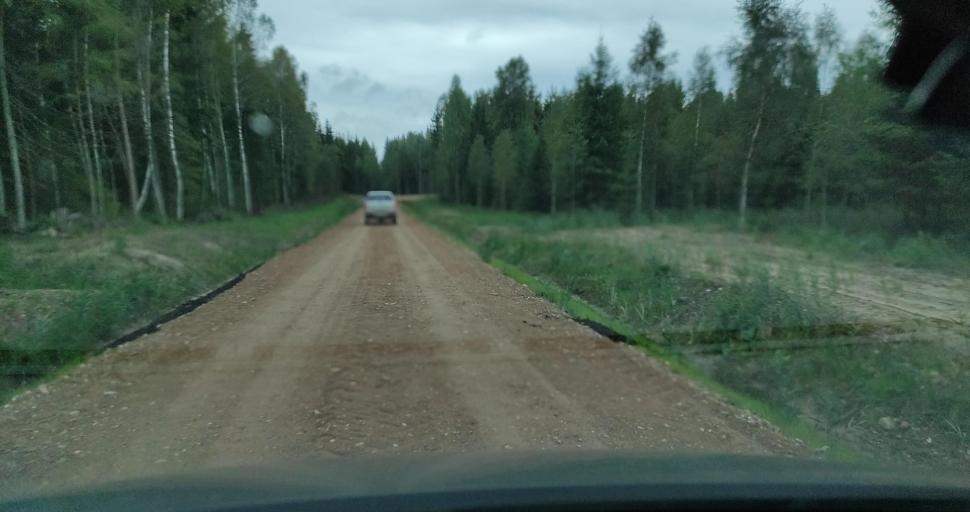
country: LV
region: Talsu Rajons
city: Sabile
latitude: 57.0158
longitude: 22.3545
